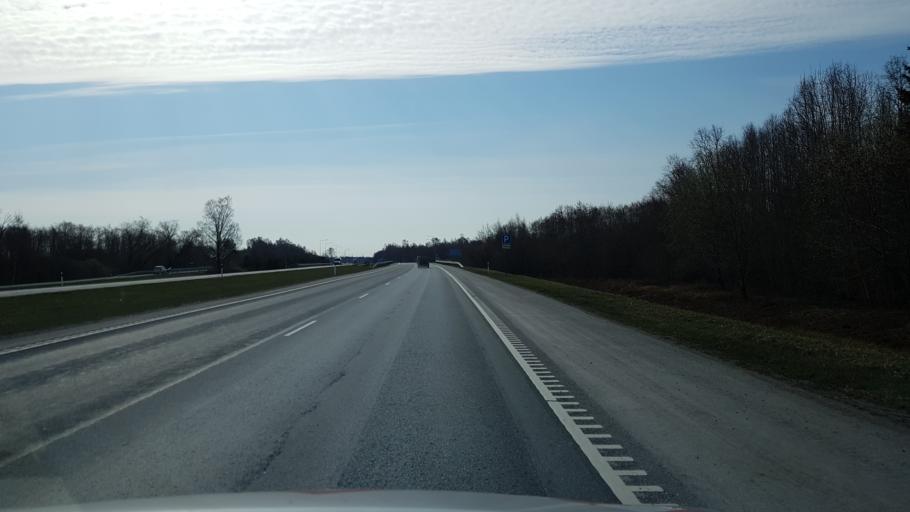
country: EE
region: Harju
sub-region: Rae vald
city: Vaida
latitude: 59.3019
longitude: 24.9471
